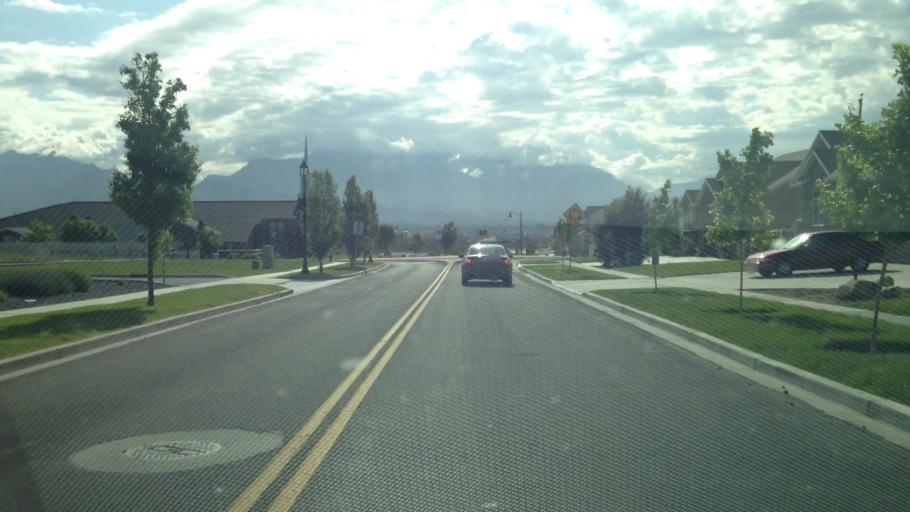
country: US
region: Utah
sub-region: Utah County
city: Saratoga Springs
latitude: 40.3916
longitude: -111.9273
